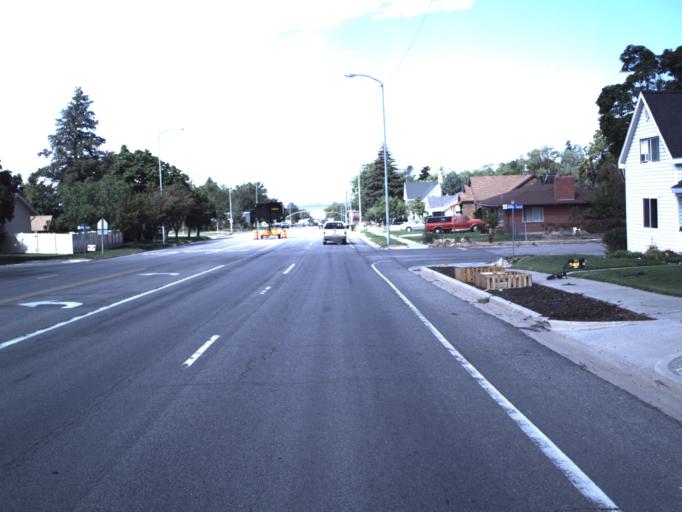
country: US
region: Utah
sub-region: Box Elder County
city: Brigham City
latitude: 41.5061
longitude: -112.0105
